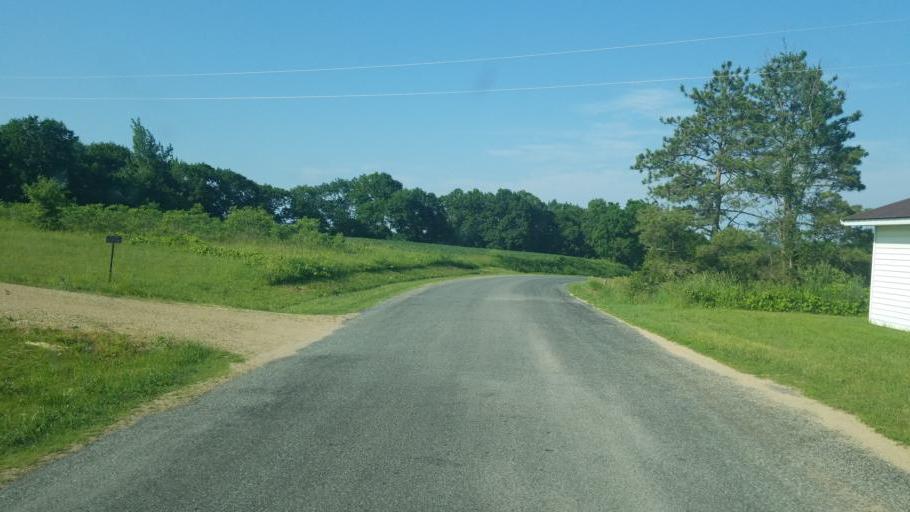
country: US
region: Wisconsin
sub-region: Vernon County
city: Hillsboro
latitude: 43.6814
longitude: -90.3729
